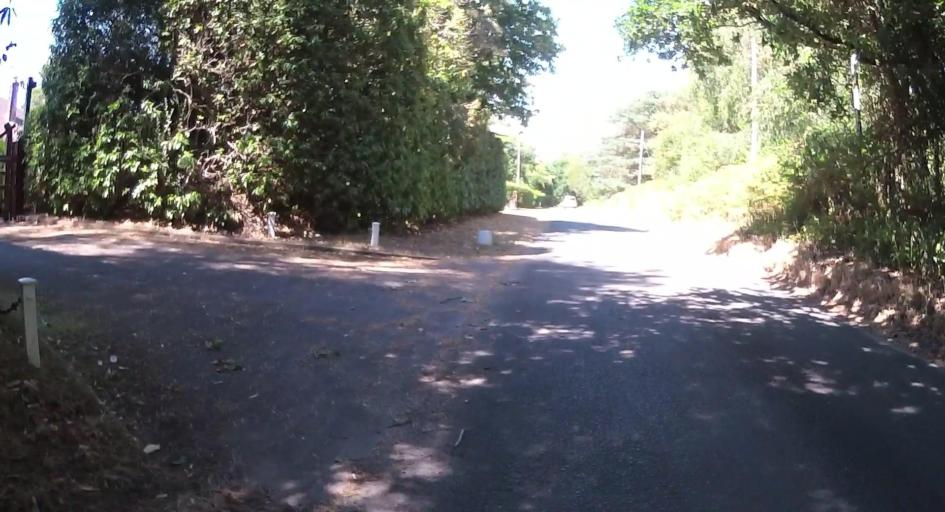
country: GB
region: England
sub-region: Dorset
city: Bovington Camp
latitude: 50.6937
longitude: -2.3008
